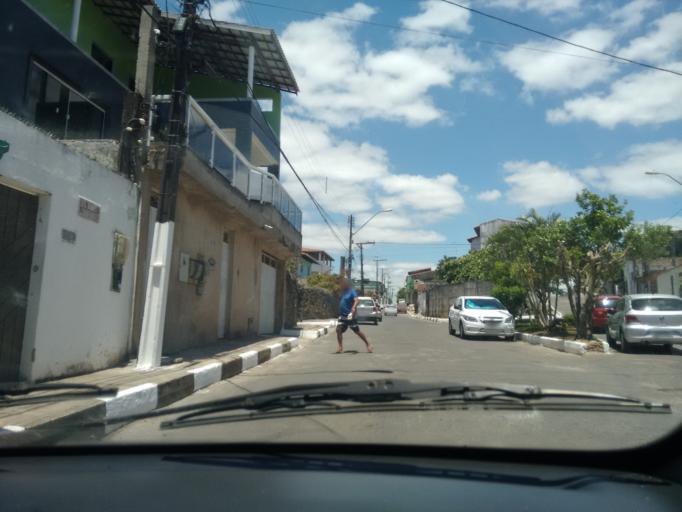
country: BR
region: Bahia
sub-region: Lauro De Freitas
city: Lauro de Freitas
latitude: -12.8949
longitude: -38.3354
